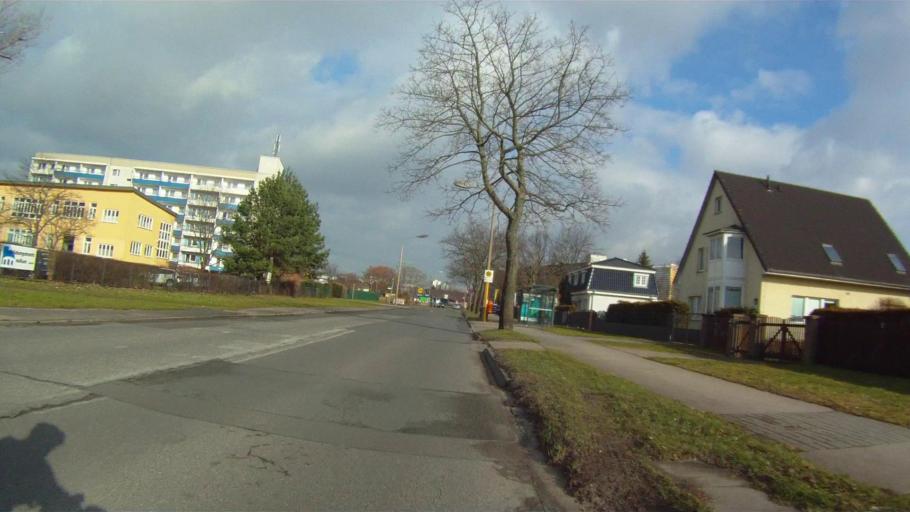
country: DE
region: Berlin
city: Biesdorf
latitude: 52.5222
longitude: 13.5329
